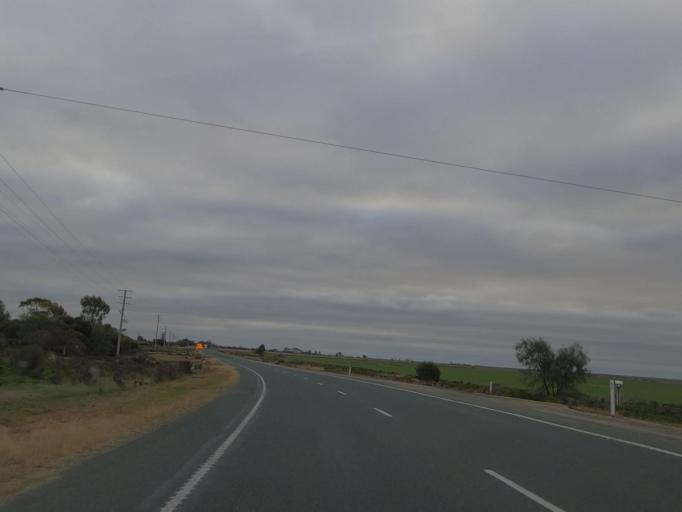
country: AU
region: Victoria
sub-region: Swan Hill
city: Swan Hill
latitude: -35.5552
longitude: 143.7766
